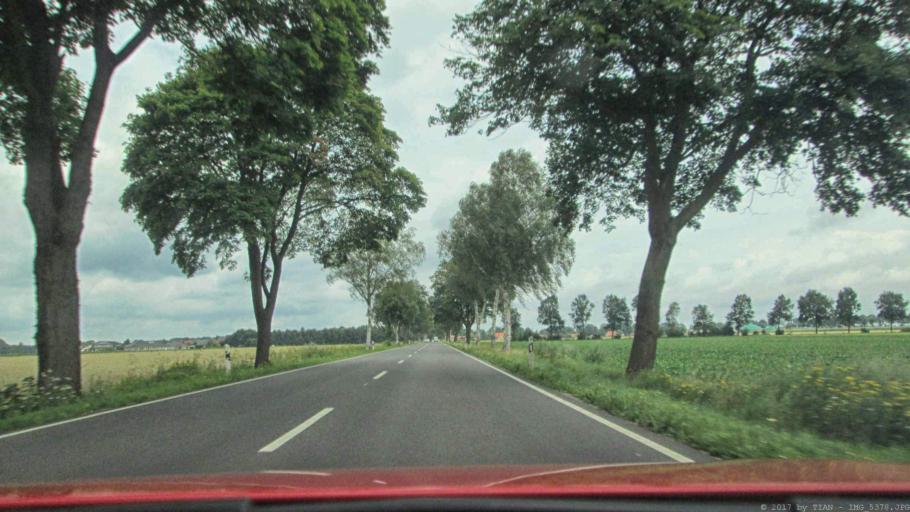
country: DE
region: Lower Saxony
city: Gross Oesingen
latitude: 52.6383
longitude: 10.4681
